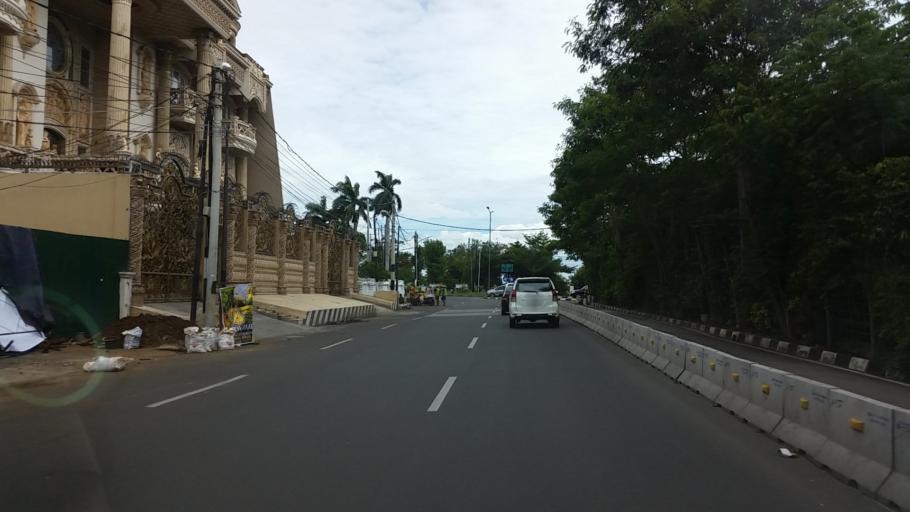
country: ID
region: Jakarta Raya
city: Jakarta
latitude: -6.1157
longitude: 106.7935
